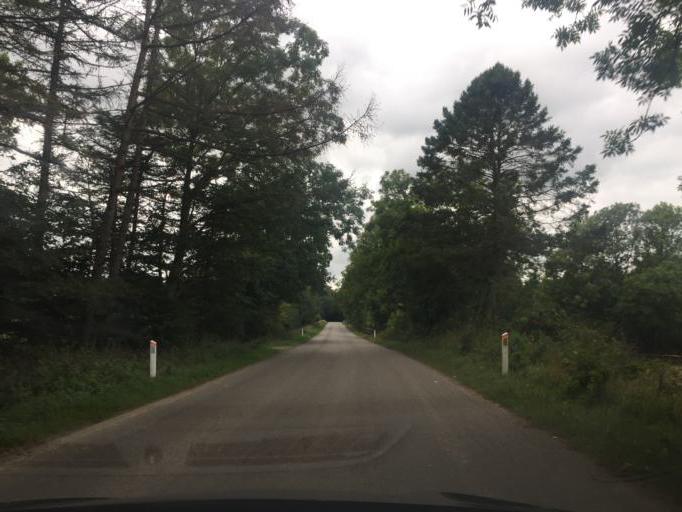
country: DK
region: South Denmark
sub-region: Assens Kommune
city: Tommerup Stationsby
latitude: 55.3557
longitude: 10.1969
